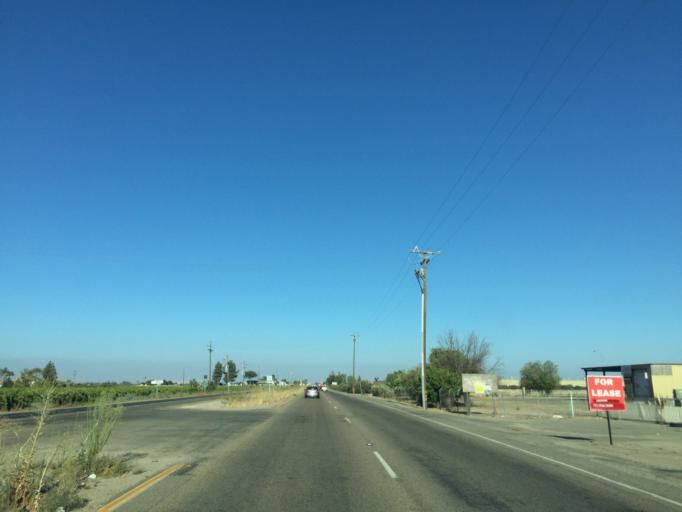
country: US
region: California
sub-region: Fresno County
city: Selma
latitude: 36.5469
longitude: -119.5899
